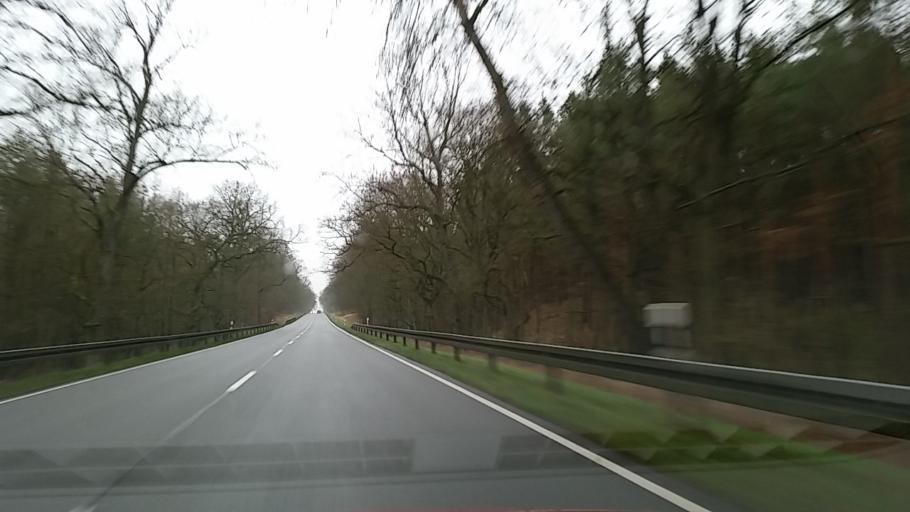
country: DE
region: Brandenburg
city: Dreetz
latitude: 52.8134
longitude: 12.5403
